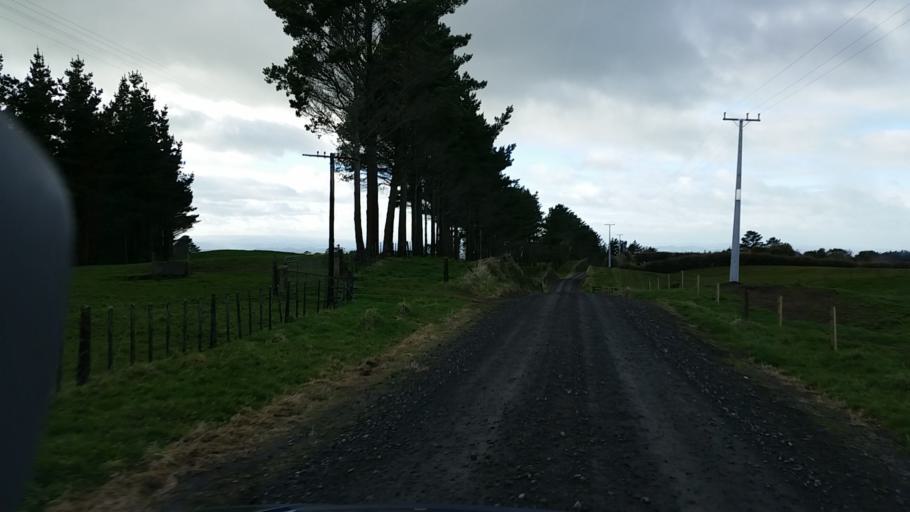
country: NZ
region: Taranaki
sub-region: South Taranaki District
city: Eltham
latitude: -39.3364
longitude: 174.1821
